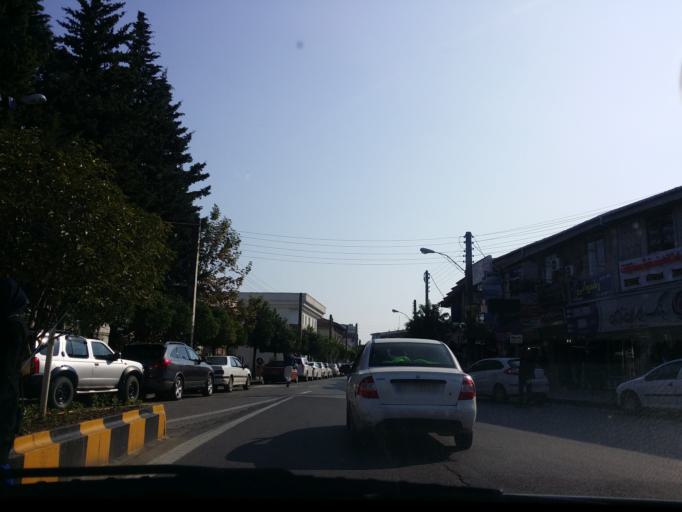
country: IR
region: Mazandaran
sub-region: Nowshahr
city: Nowshahr
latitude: 36.6509
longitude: 51.5015
